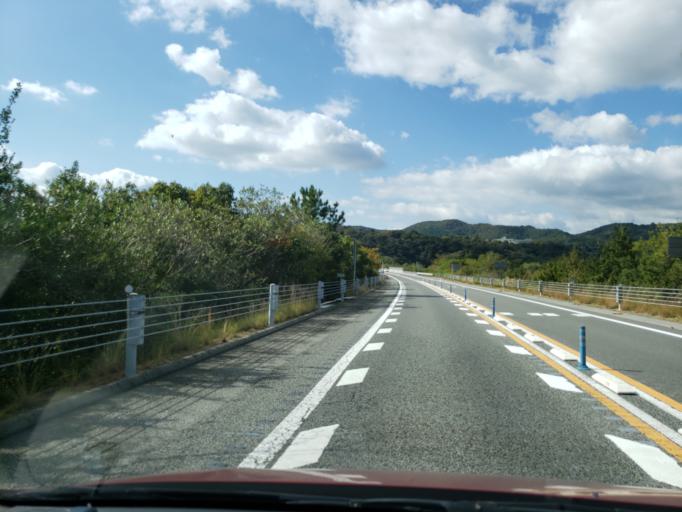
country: JP
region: Tokushima
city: Kamojimacho-jogejima
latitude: 34.1179
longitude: 134.3295
